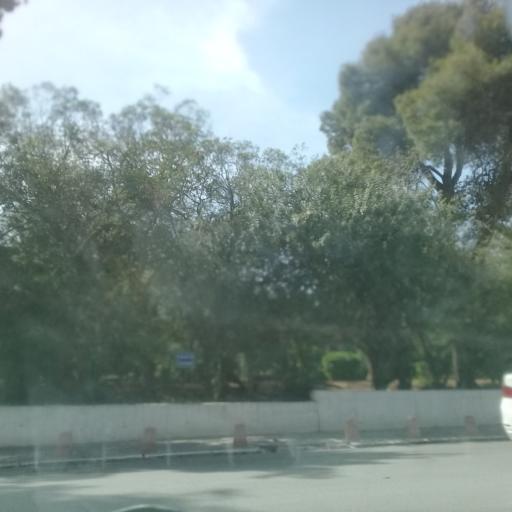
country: TN
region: Tunis
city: Tunis
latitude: 36.8186
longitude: 10.1773
